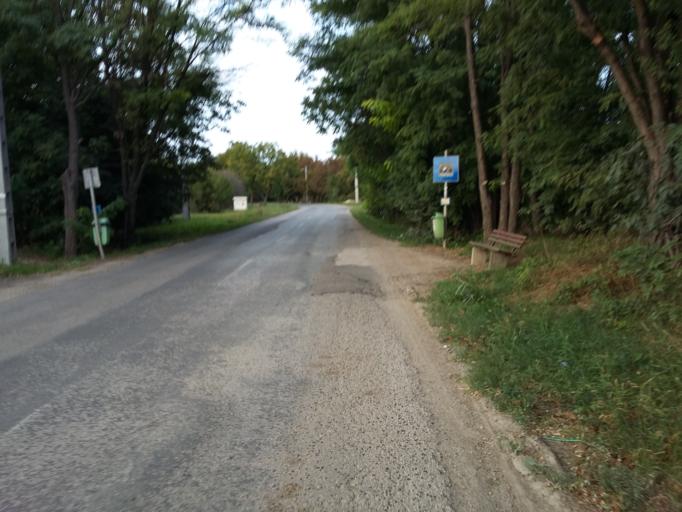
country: HU
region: Csongrad
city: Szeged
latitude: 46.2196
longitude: 20.1111
